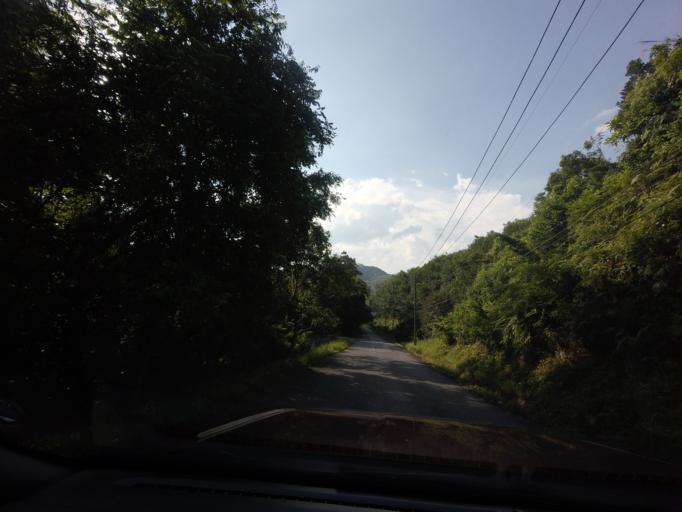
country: TH
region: Yala
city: Than To
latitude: 6.1527
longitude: 101.2810
